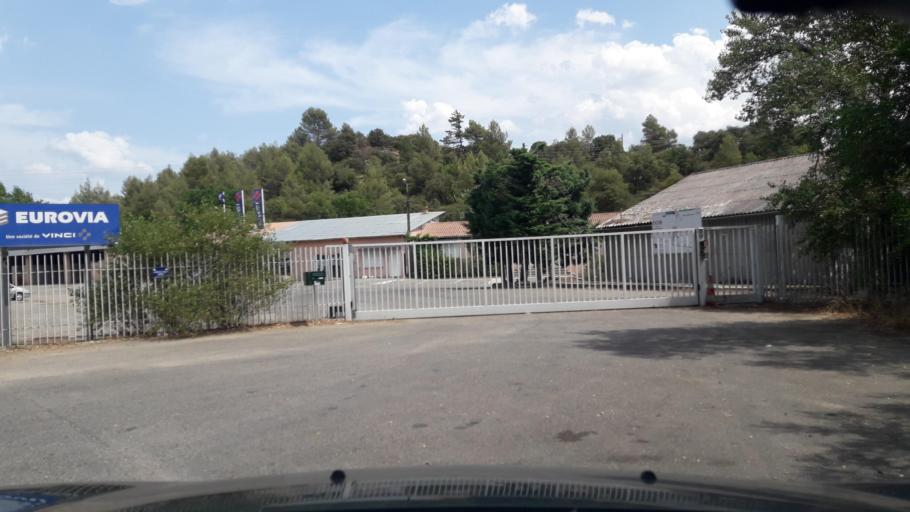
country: FR
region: Provence-Alpes-Cote d'Azur
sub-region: Departement du Var
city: Vinon-sur-Verdon
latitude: 43.7330
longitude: 5.8310
